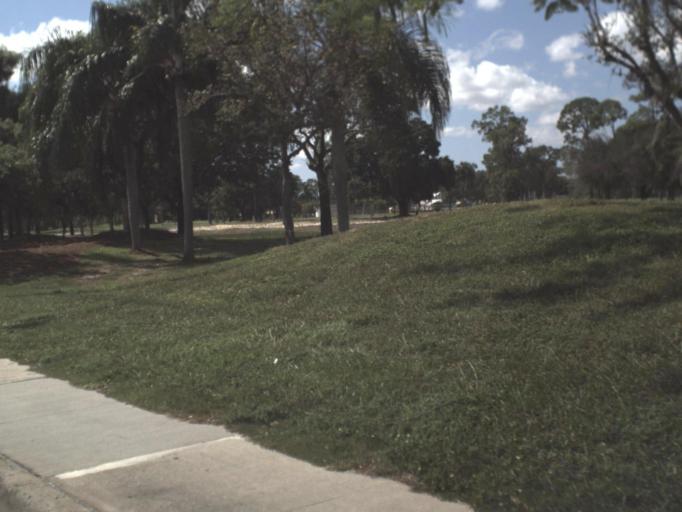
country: US
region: Florida
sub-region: Lee County
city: Fort Myers
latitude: 26.6136
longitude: -81.8722
